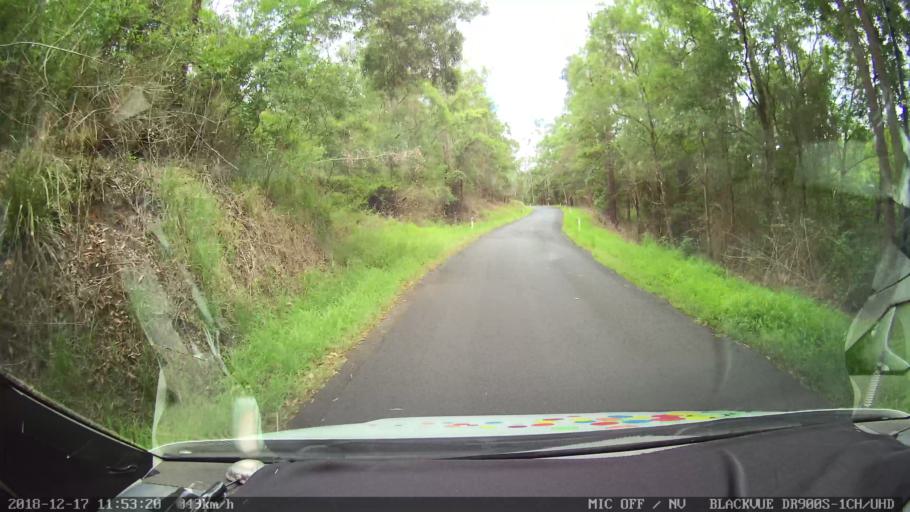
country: AU
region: New South Wales
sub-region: Kyogle
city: Kyogle
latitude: -28.5750
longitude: 152.5866
